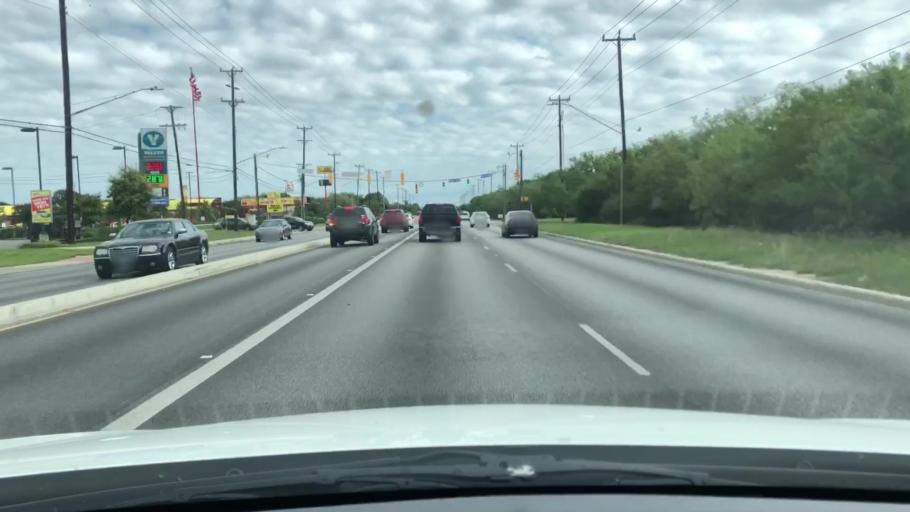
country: US
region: Texas
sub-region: Bexar County
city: Leon Valley
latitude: 29.4894
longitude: -98.6785
